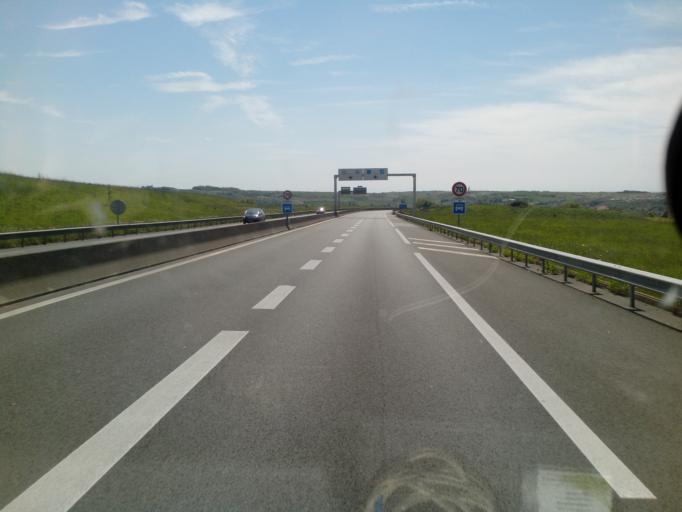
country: FR
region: Nord-Pas-de-Calais
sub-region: Departement du Pas-de-Calais
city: Saint-Leonard
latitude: 50.7060
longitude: 1.6321
